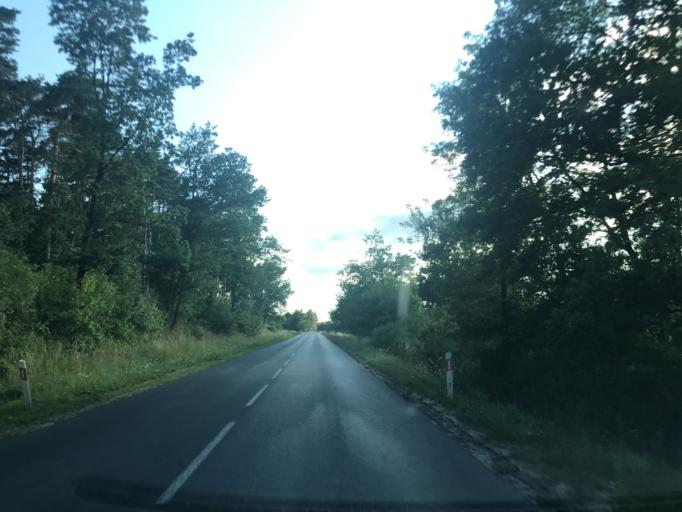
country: PL
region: Greater Poland Voivodeship
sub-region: Powiat jarocinski
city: Jarocin
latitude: 51.9844
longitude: 17.5386
